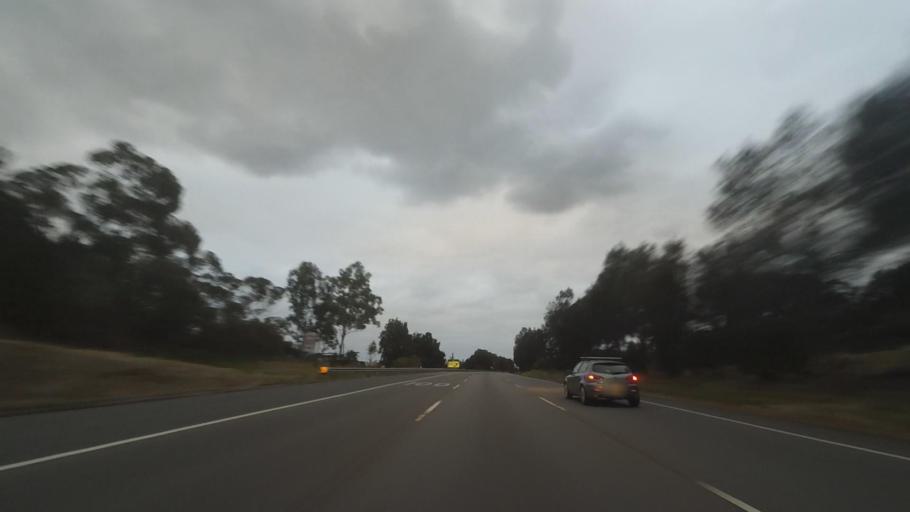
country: AU
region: New South Wales
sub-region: Wollongong
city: Berkeley
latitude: -34.4695
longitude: 150.8367
